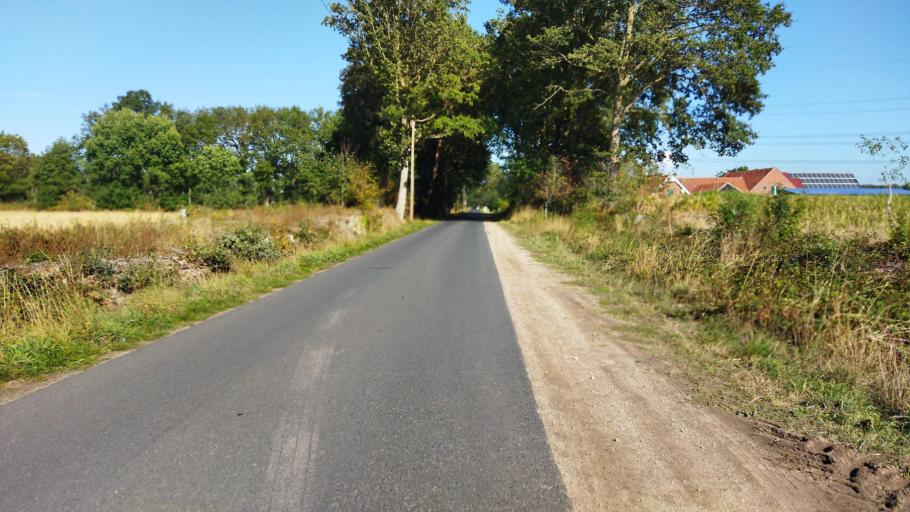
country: DE
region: North Rhine-Westphalia
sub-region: Regierungsbezirk Munster
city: Wettringen
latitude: 52.2353
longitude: 7.3124
